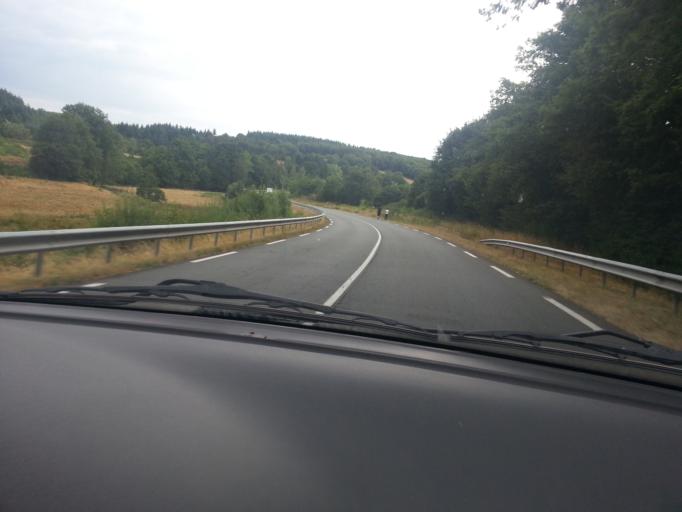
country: FR
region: Auvergne
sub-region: Departement de l'Allier
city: Lapalisse
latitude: 46.2639
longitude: 3.7282
